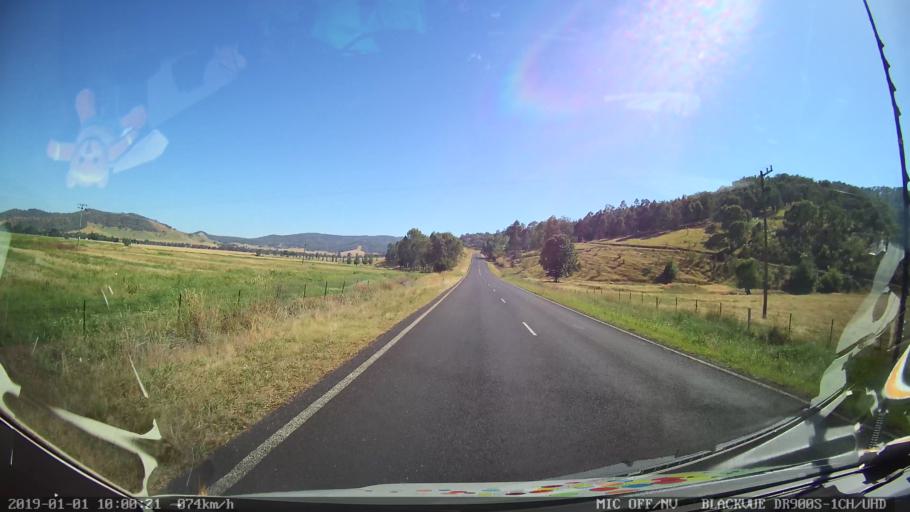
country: AU
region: New South Wales
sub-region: Snowy River
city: Jindabyne
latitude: -36.2032
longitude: 148.1016
